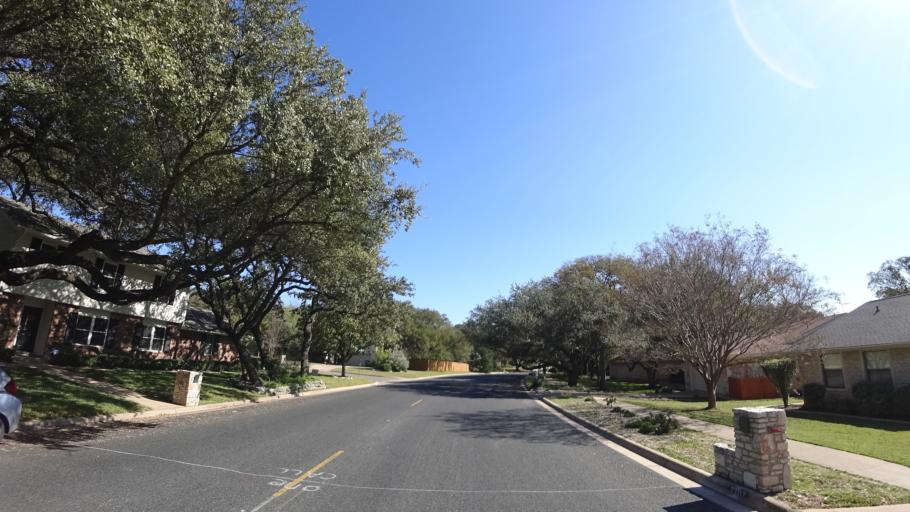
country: US
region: Texas
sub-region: Williamson County
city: Jollyville
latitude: 30.4249
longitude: -97.7681
